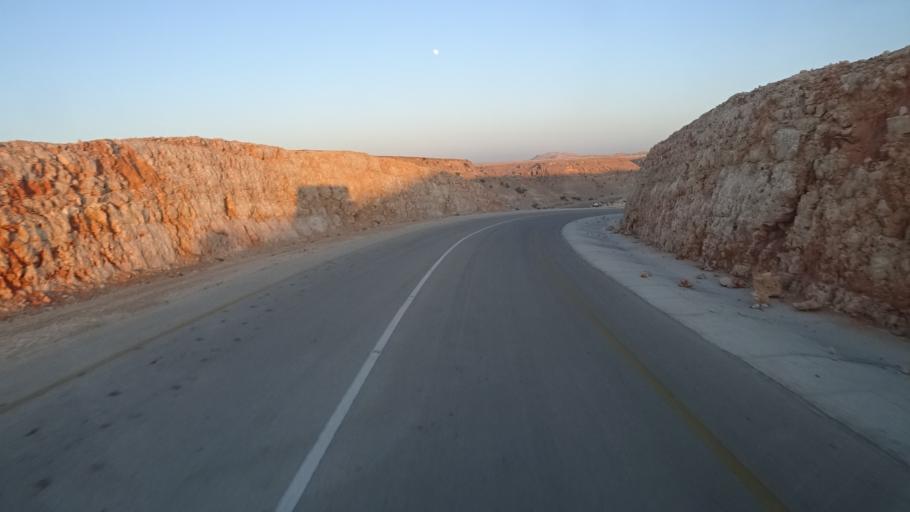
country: YE
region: Al Mahrah
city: Hawf
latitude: 16.9558
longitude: 53.3309
